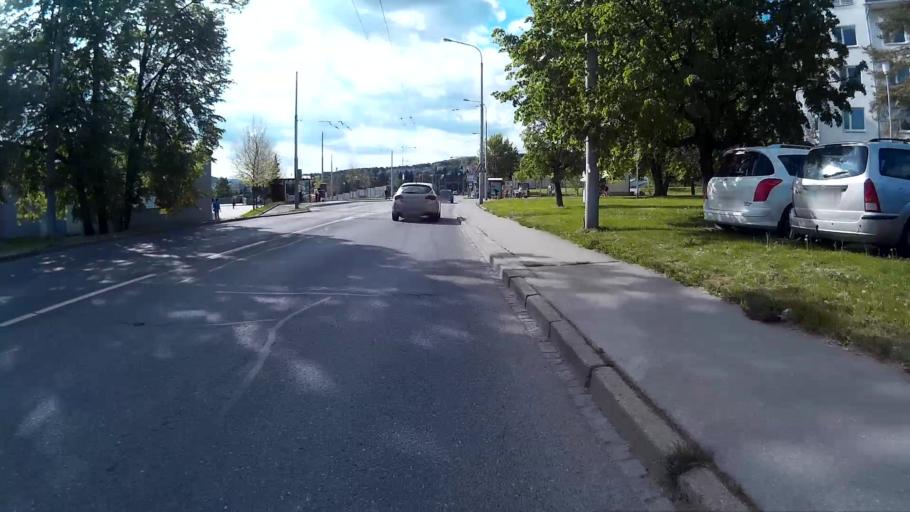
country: CZ
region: South Moravian
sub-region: Mesto Brno
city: Brno
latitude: 49.2155
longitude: 16.5824
